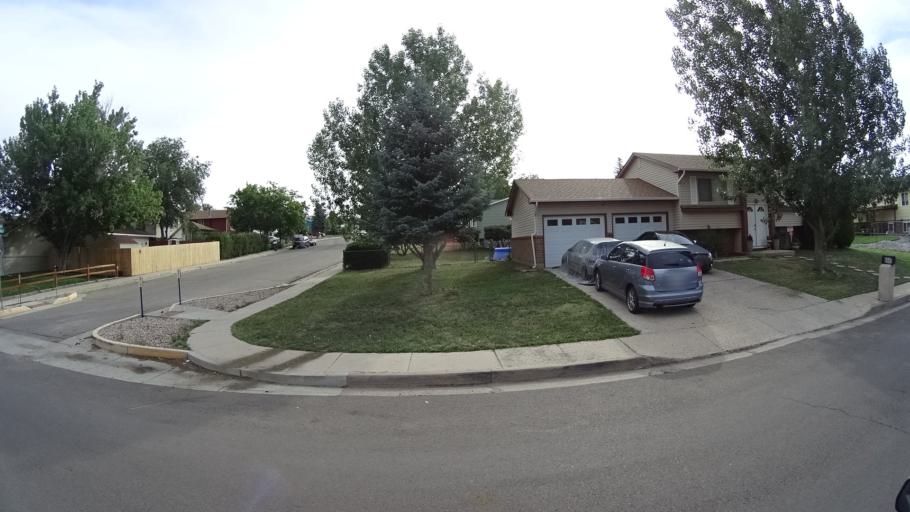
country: US
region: Colorado
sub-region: El Paso County
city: Security-Widefield
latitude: 38.7315
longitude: -104.6930
